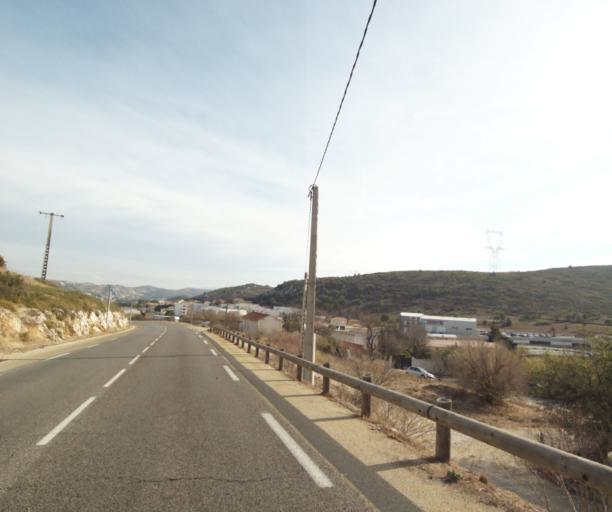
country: FR
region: Provence-Alpes-Cote d'Azur
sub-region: Departement des Bouches-du-Rhone
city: Le Rove
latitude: 43.3627
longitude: 5.2362
